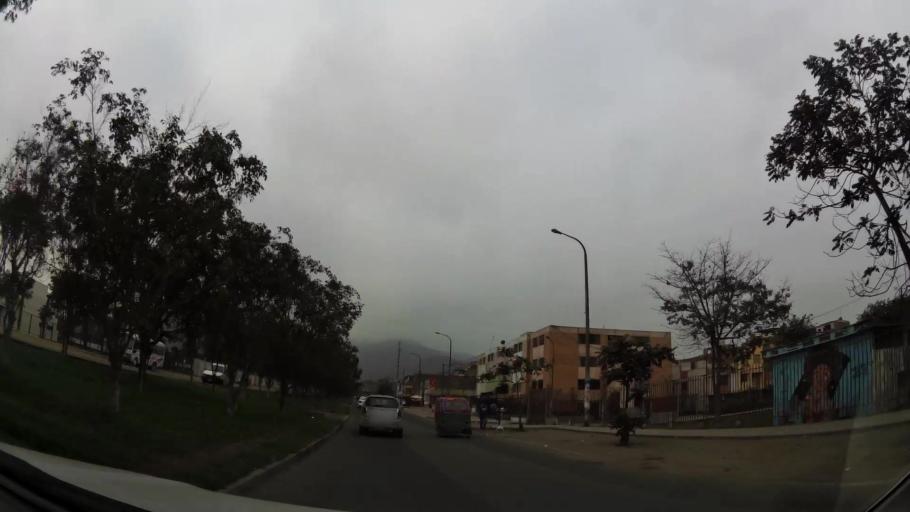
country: PE
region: Lima
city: Lima
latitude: -12.0129
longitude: -77.0007
